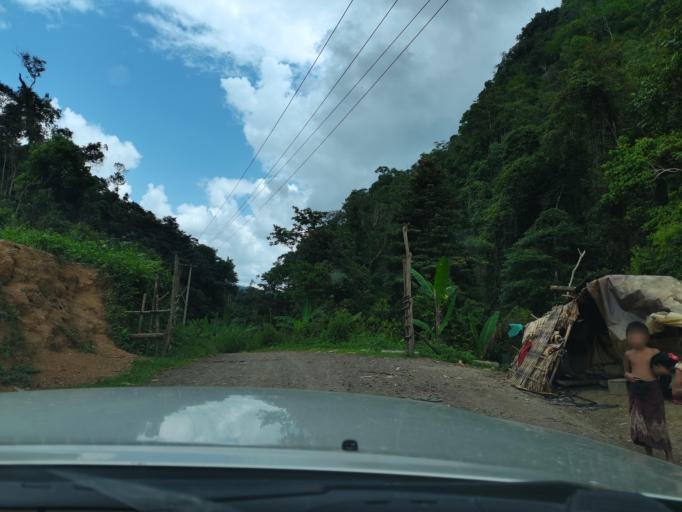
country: LA
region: Loungnamtha
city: Muang Long
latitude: 20.7780
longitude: 101.0167
